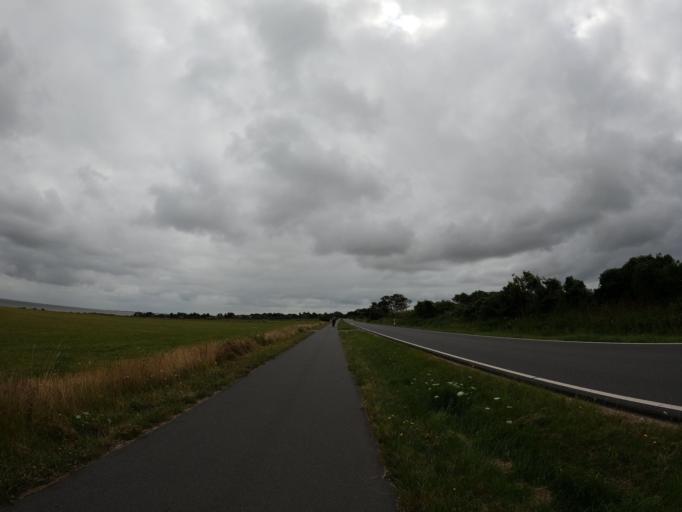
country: DE
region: Schleswig-Holstein
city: Tinnum
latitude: 54.9387
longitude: 8.3491
